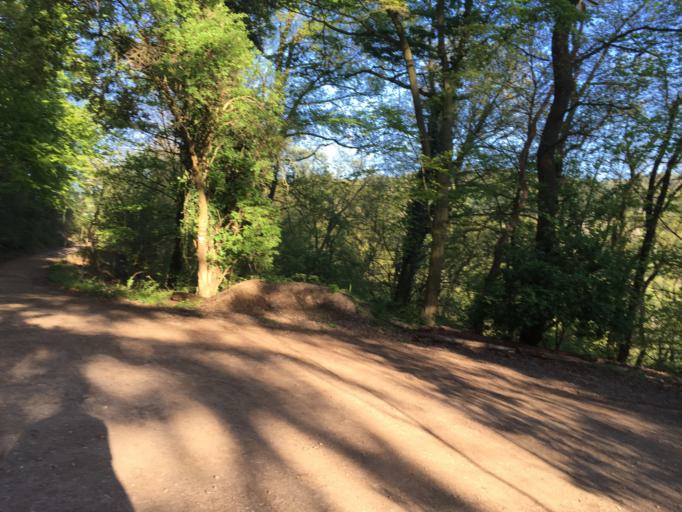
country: DE
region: Baden-Wuerttemberg
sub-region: Karlsruhe Region
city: Schriesheim
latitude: 49.5107
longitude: 8.6739
